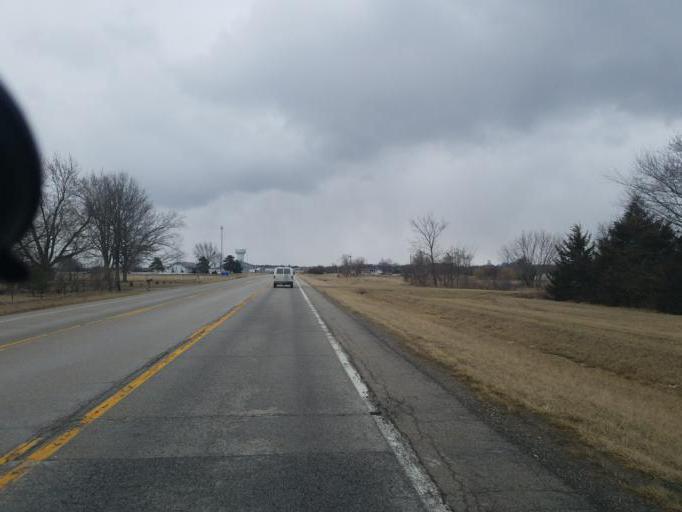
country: US
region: Missouri
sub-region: Macon County
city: Macon
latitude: 39.7694
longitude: -92.4717
